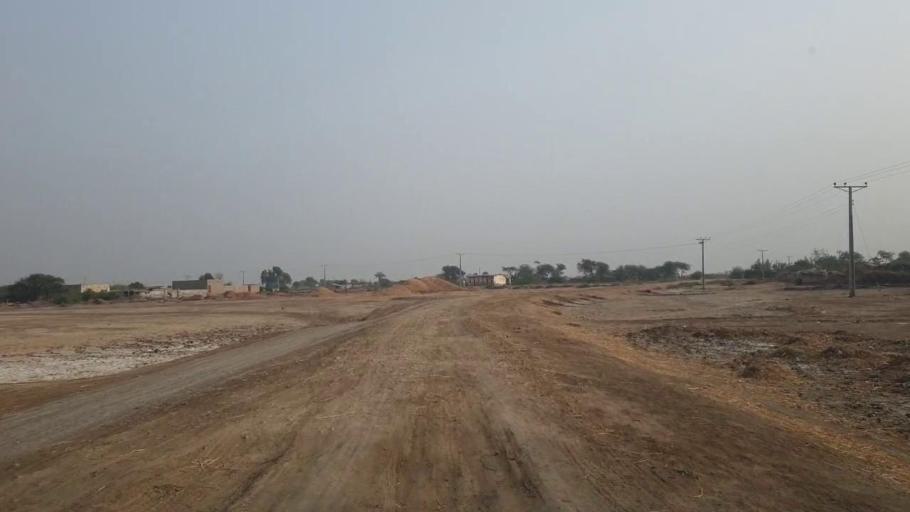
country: PK
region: Sindh
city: Mirpur Batoro
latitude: 24.5583
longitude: 68.4209
